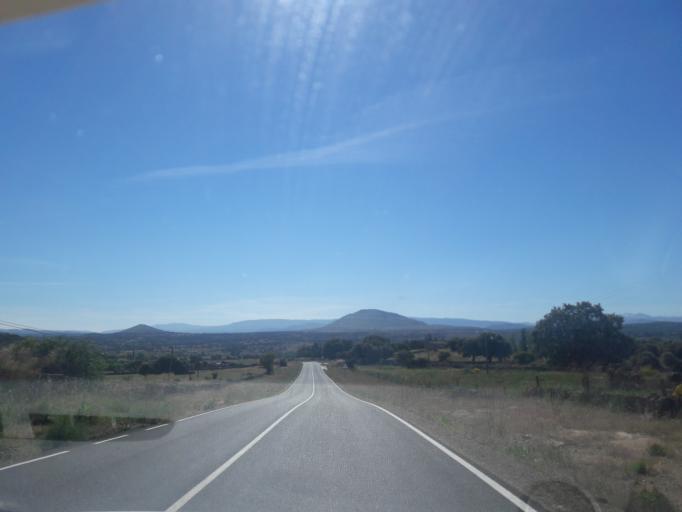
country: ES
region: Castille and Leon
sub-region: Provincia de Salamanca
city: Santibanez de Bejar
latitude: 40.4812
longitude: -5.6418
